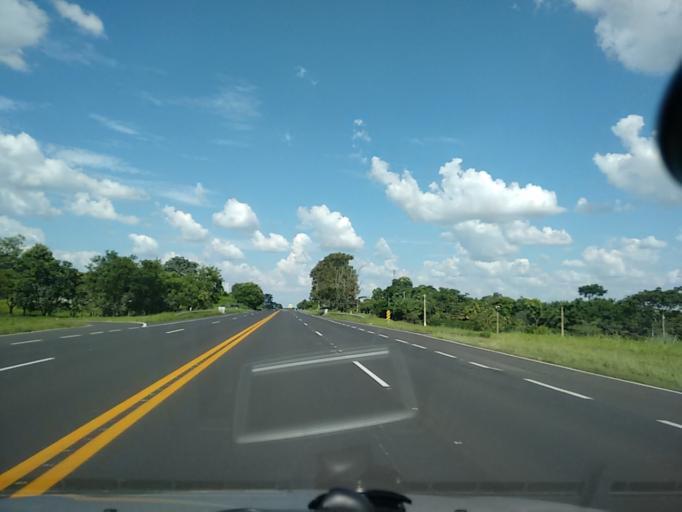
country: BR
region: Sao Paulo
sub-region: Marilia
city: Marilia
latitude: -22.1572
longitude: -50.0113
